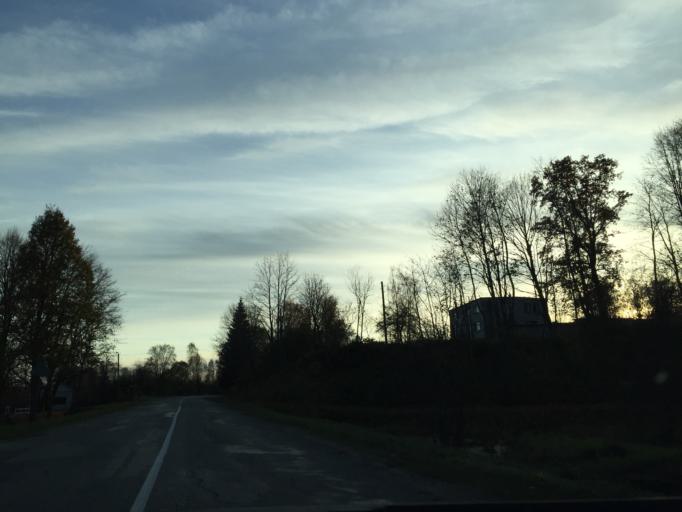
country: LV
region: Jaunjelgava
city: Jaunjelgava
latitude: 56.6309
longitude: 25.0966
